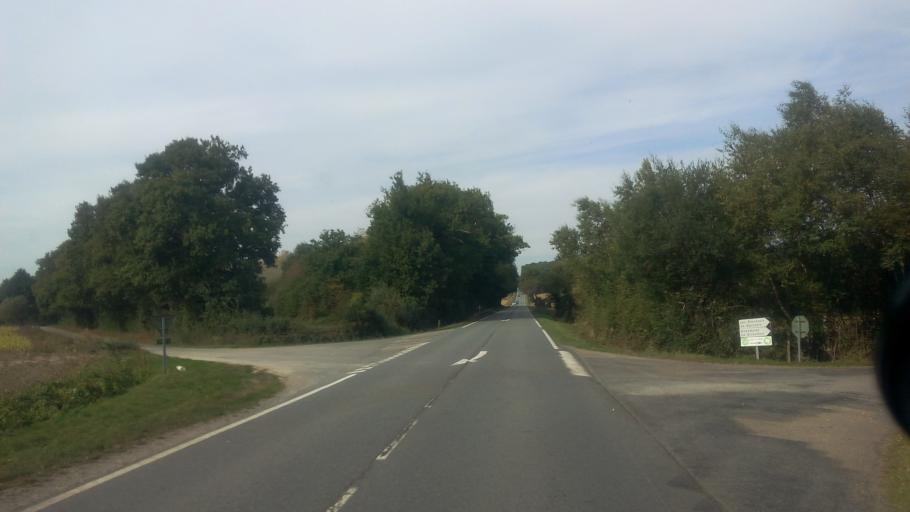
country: FR
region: Brittany
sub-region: Departement d'Ille-et-Vilaine
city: Bains-sur-Oust
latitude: 47.7177
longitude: -2.0939
